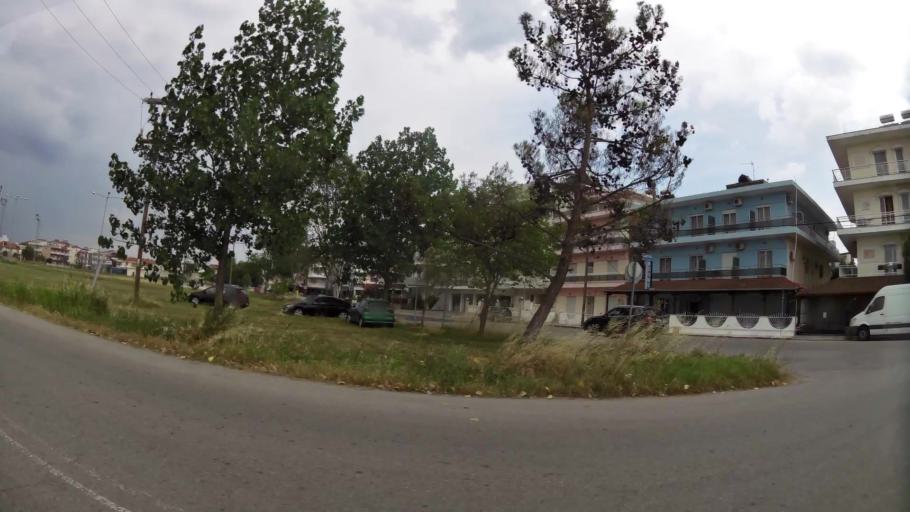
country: GR
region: Central Macedonia
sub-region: Nomos Pierias
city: Paralia
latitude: 40.2701
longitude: 22.5942
